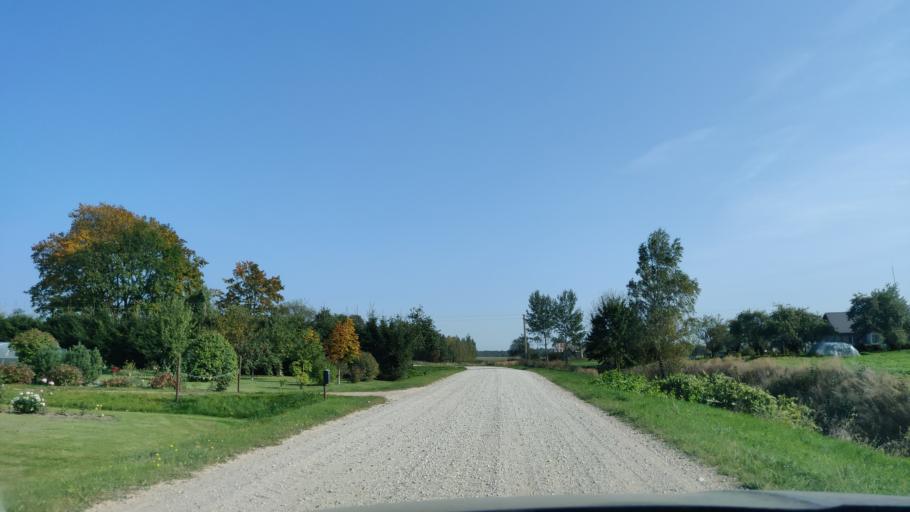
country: LT
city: Sirvintos
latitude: 54.9708
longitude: 24.8332
